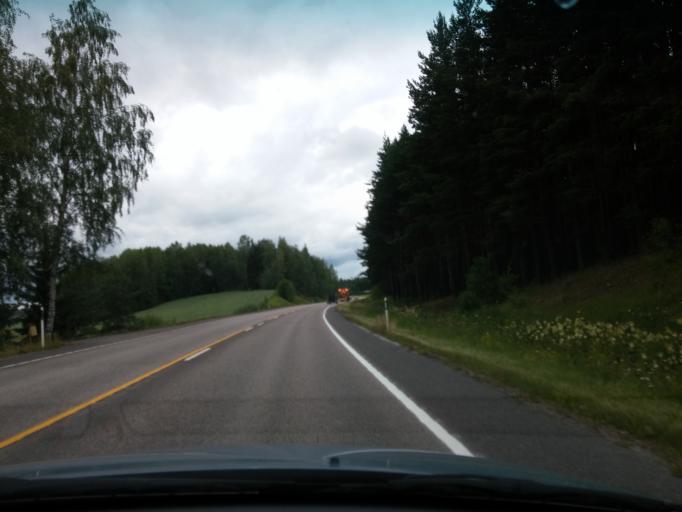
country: FI
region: Uusimaa
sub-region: Porvoo
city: Askola
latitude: 60.4704
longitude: 25.5697
